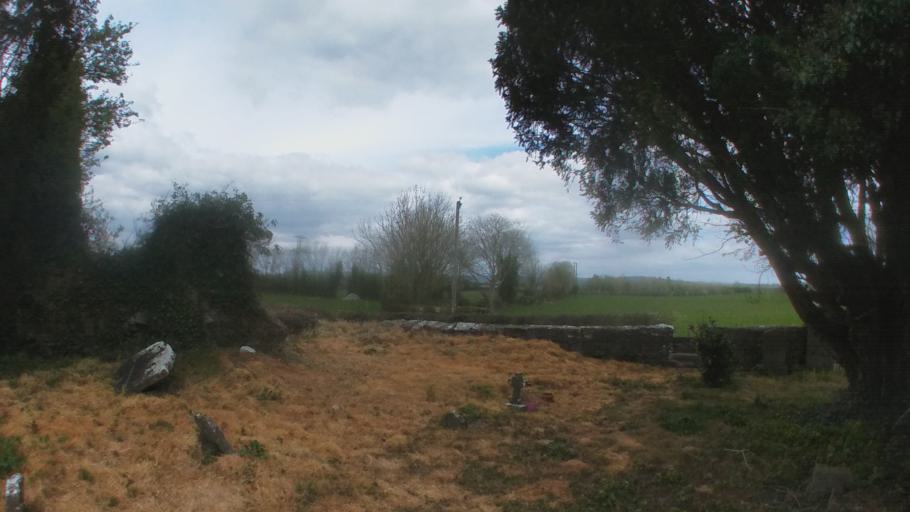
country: IE
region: Leinster
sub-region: Kilkenny
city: Kilkenny
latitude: 52.6525
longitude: -7.1884
